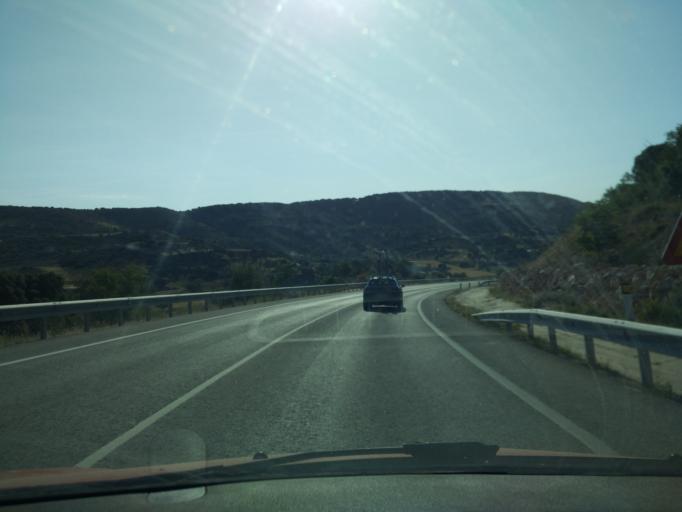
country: ES
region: Madrid
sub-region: Provincia de Madrid
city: Villar del Olmo
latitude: 40.3322
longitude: -3.2311
